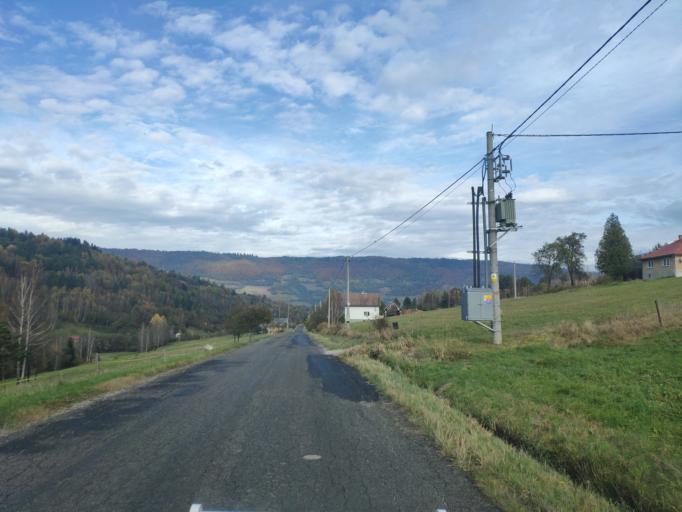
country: SK
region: Kosicky
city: Spisska Nova Ves
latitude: 48.8242
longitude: 20.6247
